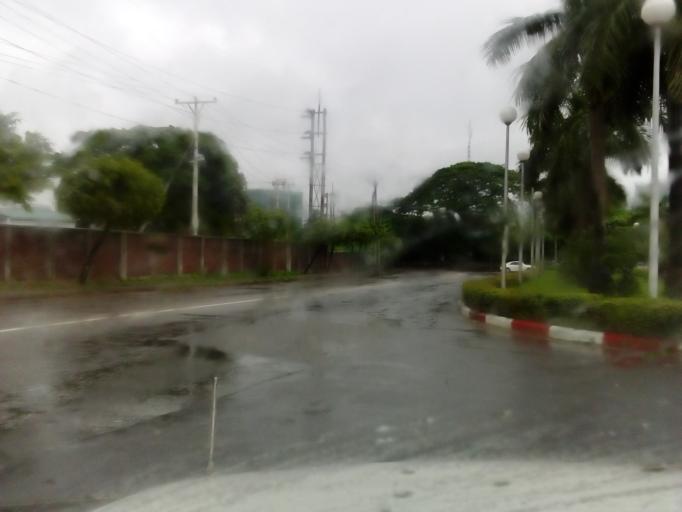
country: MM
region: Yangon
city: Yangon
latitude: 16.8242
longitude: 96.1718
